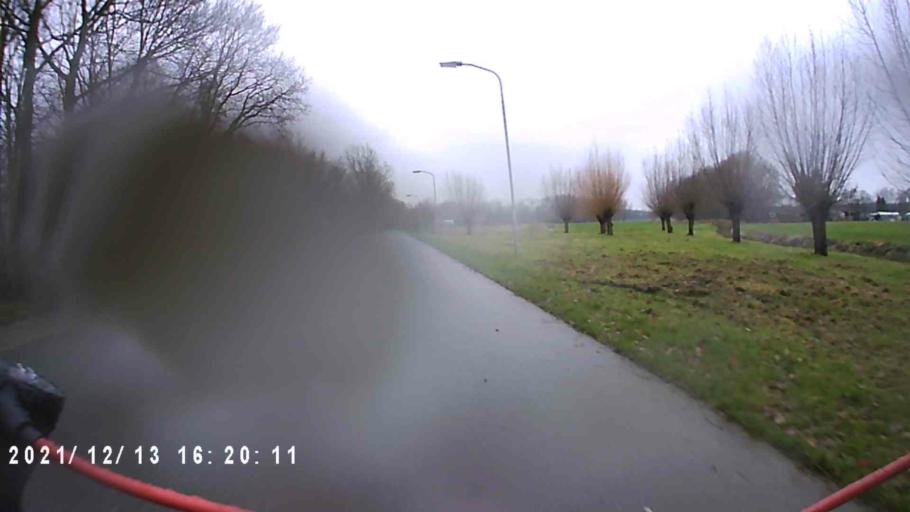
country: NL
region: Groningen
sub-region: Gemeente Delfzijl
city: Delfzijl
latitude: 53.3382
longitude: 6.8964
